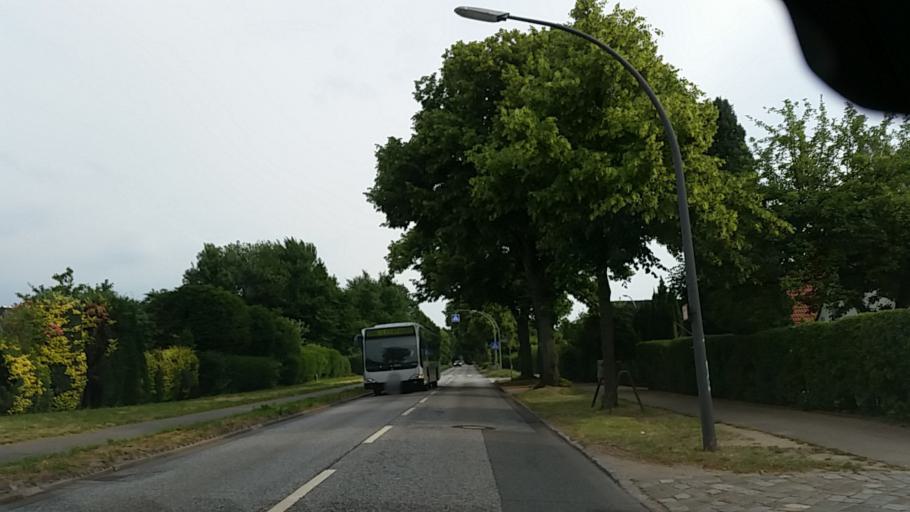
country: DE
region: Schleswig-Holstein
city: Halstenbek
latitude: 53.5815
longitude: 9.8228
